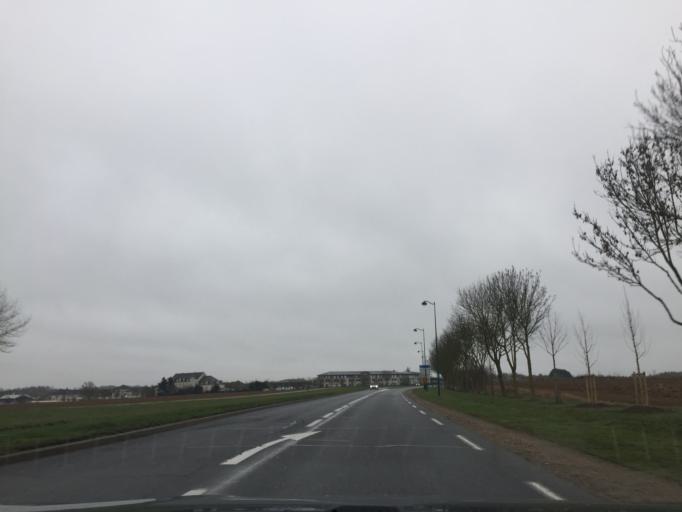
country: FR
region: Ile-de-France
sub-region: Departement de Seine-et-Marne
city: Magny-le-Hongre
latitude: 48.8704
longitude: 2.8063
